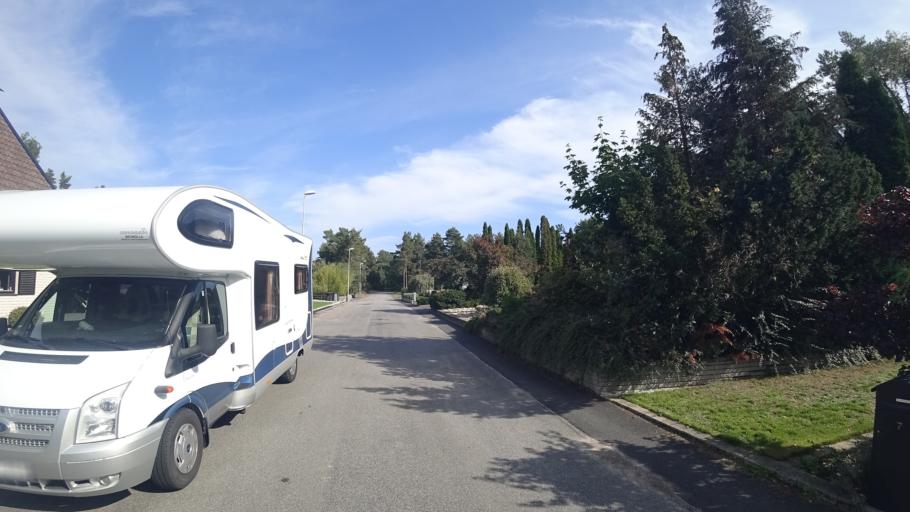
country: SE
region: Skane
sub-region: Kristianstads Kommun
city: Ahus
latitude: 55.9129
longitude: 14.2843
